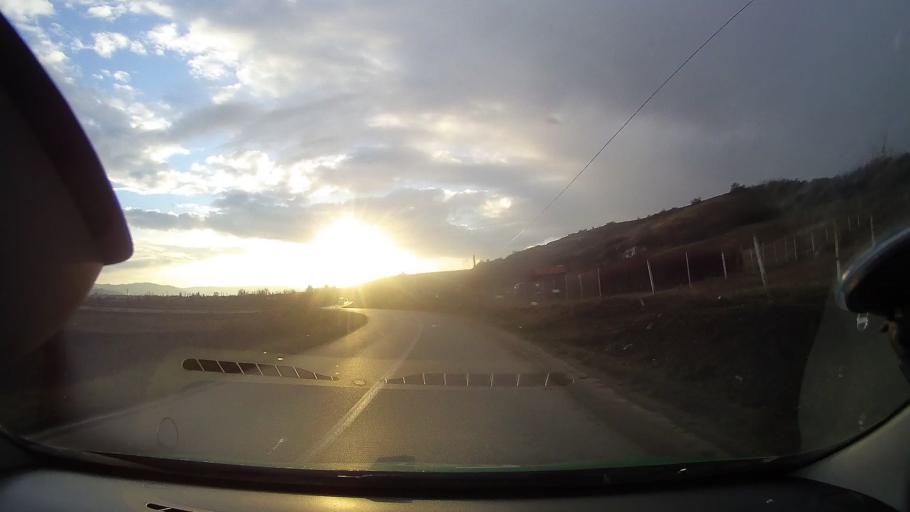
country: RO
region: Alba
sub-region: Oras Ocna Mures
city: Razboieni-Cetate
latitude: 46.4236
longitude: 23.8814
